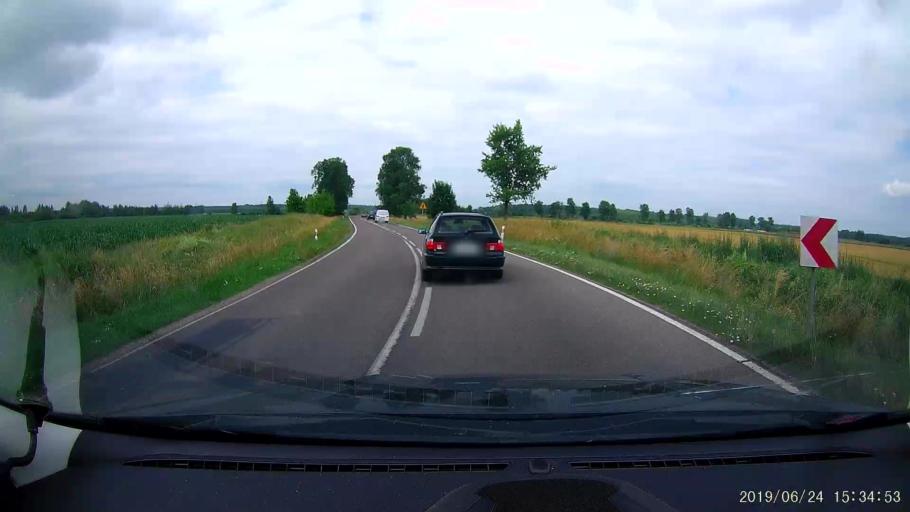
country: PL
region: Subcarpathian Voivodeship
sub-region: Powiat jaroslawski
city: Wiazownica
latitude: 50.0614
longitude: 22.7868
